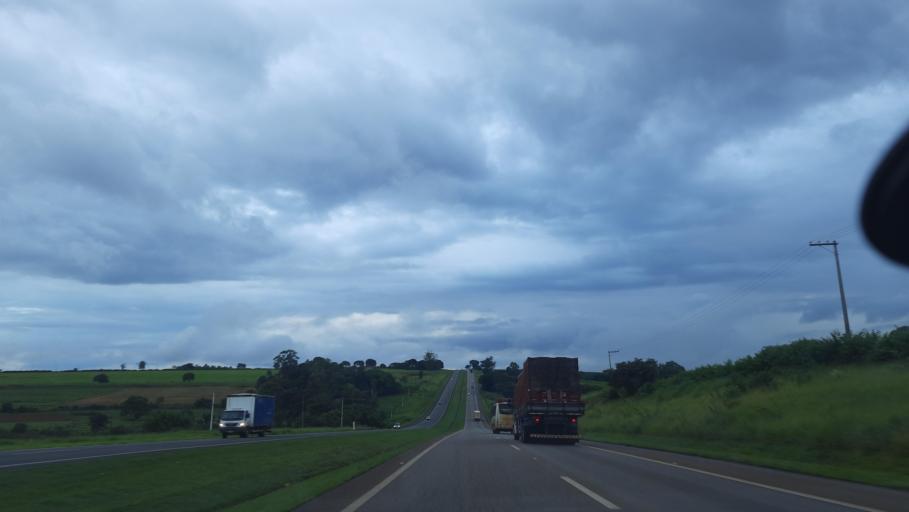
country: BR
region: Sao Paulo
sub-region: Moji-Guacu
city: Mogi-Gaucu
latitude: -22.2441
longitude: -46.9781
